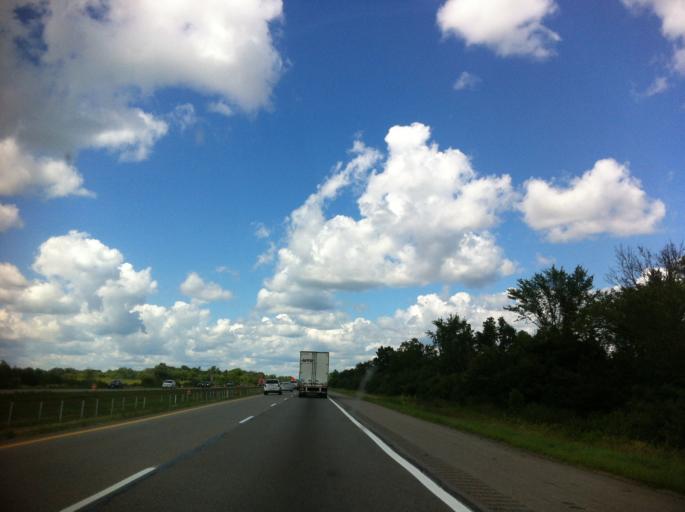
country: US
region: Michigan
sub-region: Washtenaw County
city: Ypsilanti
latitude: 42.1914
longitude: -83.6845
